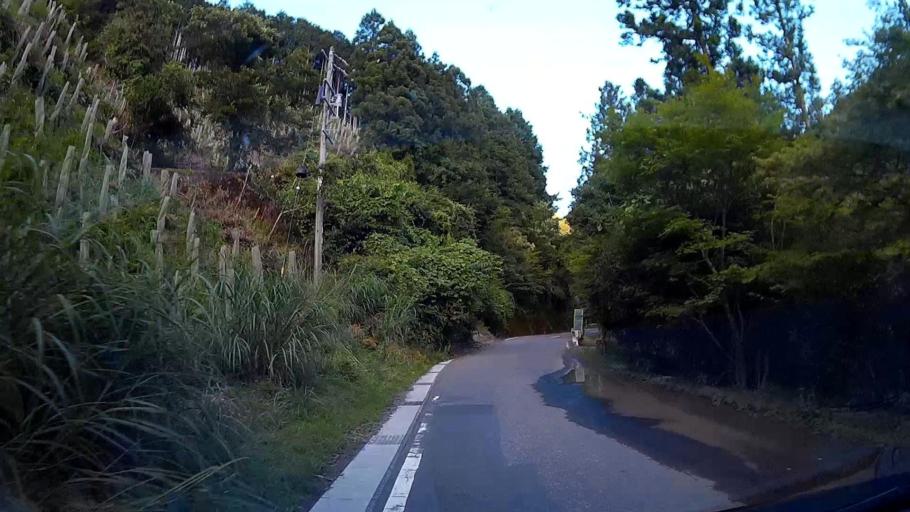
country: JP
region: Shizuoka
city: Shizuoka-shi
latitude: 35.1501
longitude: 138.2625
